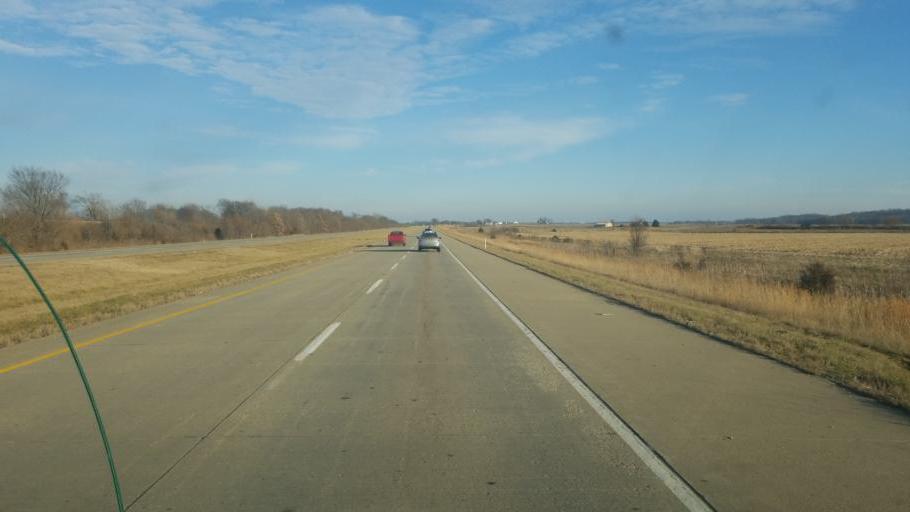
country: US
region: Indiana
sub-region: Knox County
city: Bicknell
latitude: 38.6770
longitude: -87.3845
